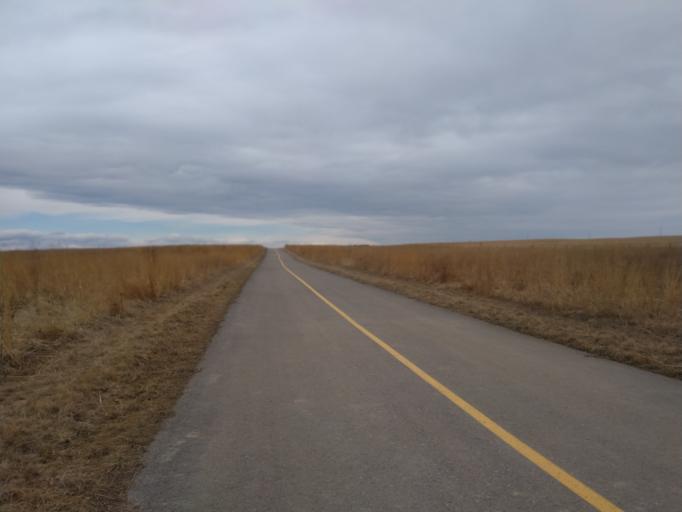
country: CA
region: Alberta
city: Airdrie
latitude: 51.1779
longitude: -114.0305
